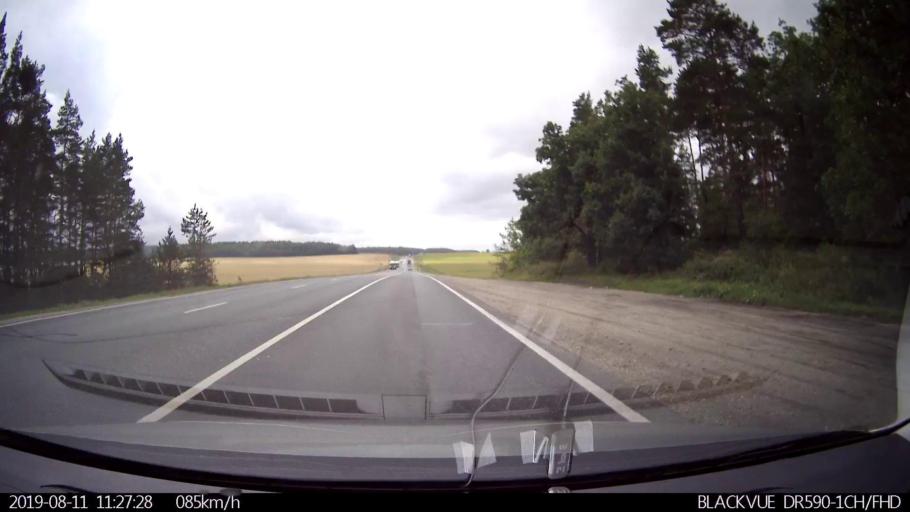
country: RU
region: Ulyanovsk
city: Krasnyy Gulyay
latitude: 54.0926
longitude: 48.2315
